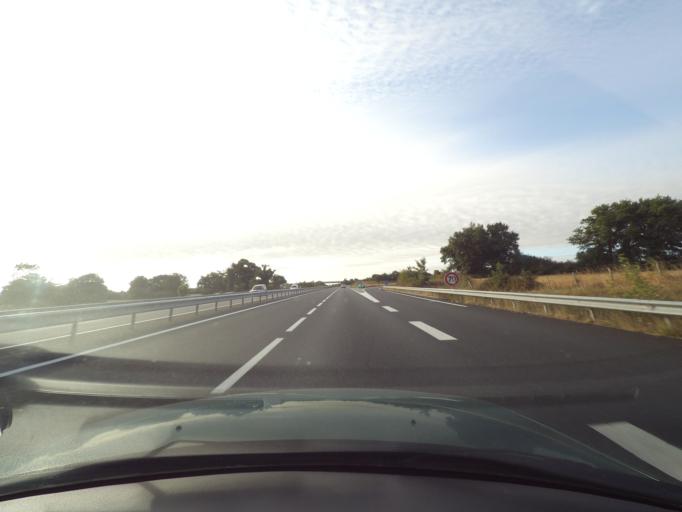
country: FR
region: Pays de la Loire
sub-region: Departement de Maine-et-Loire
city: La Tessoualle
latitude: 46.9908
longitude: -0.8477
